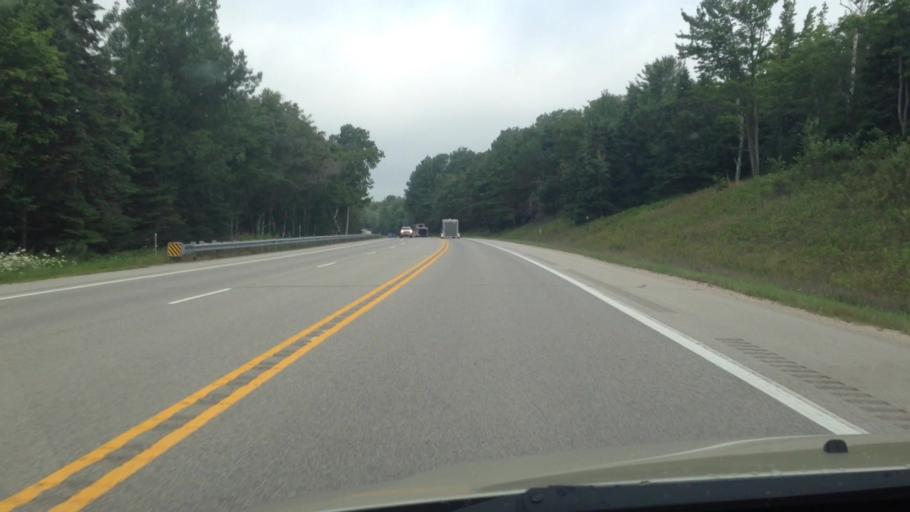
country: US
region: Michigan
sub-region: Luce County
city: Newberry
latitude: 46.0692
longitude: -85.1983
